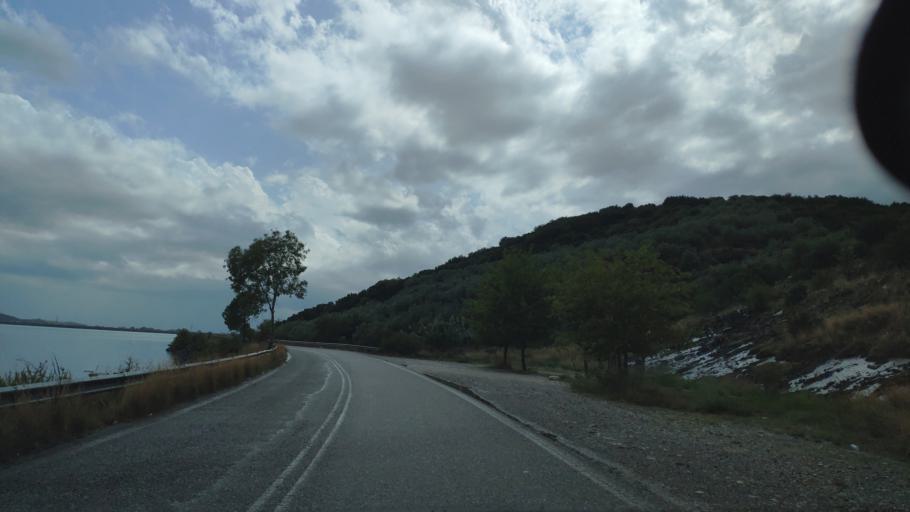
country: GR
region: West Greece
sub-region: Nomos Aitolias kai Akarnanias
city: Lepenou
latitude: 38.6901
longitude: 21.3213
